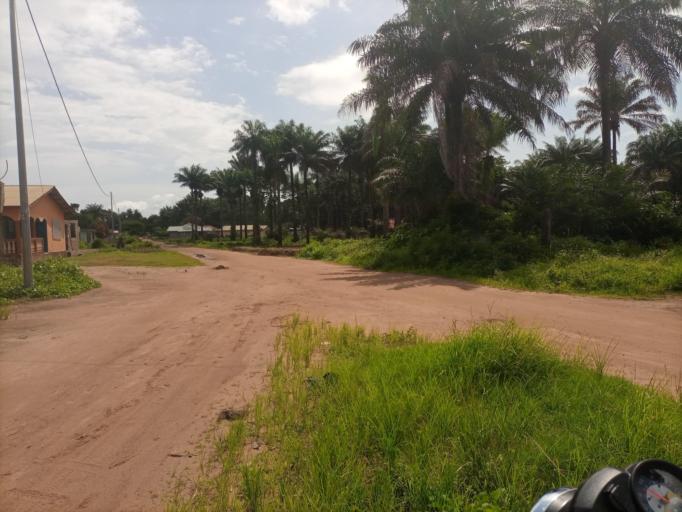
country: SL
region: Northern Province
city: Tintafor
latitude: 8.6374
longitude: -13.2177
